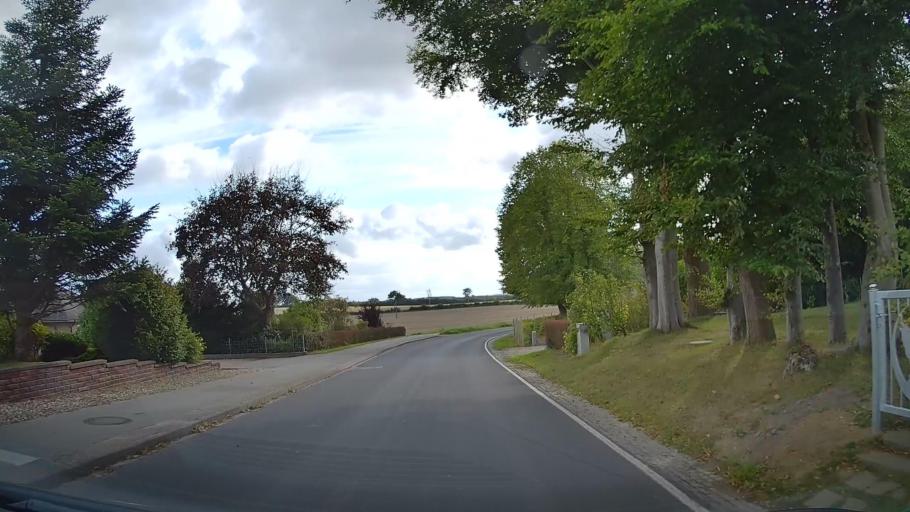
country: DE
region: Schleswig-Holstein
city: Niesgrau
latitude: 54.7672
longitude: 9.8068
